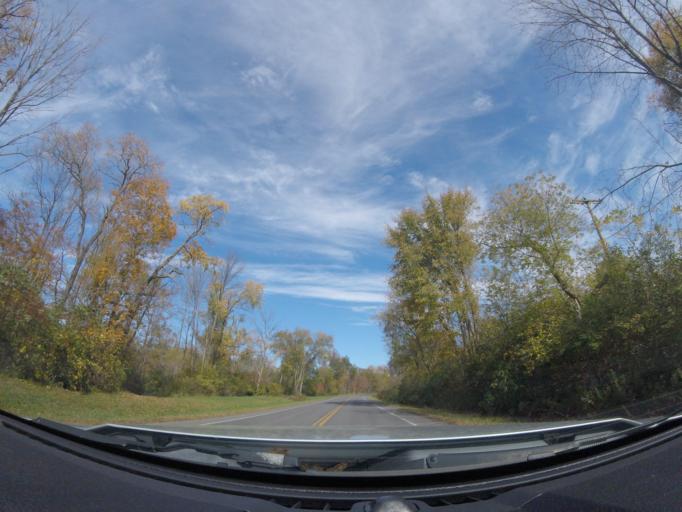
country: US
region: New York
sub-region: Tompkins County
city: Dryden
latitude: 42.5237
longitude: -76.3241
